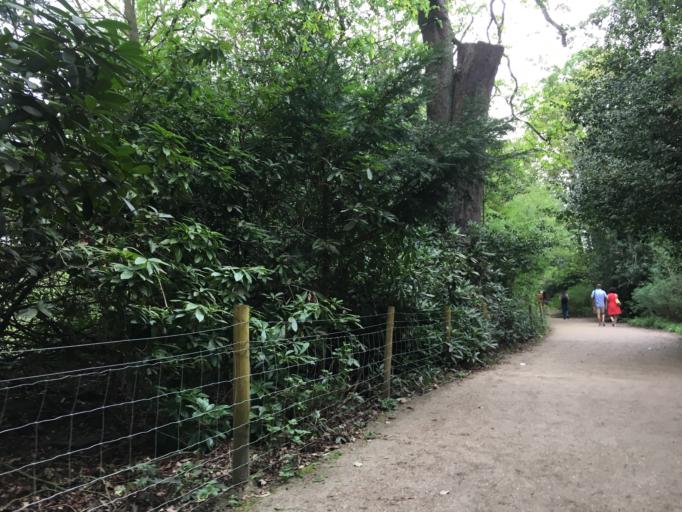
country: GB
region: England
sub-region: Greater London
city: Belsize Park
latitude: 51.5688
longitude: -0.1643
